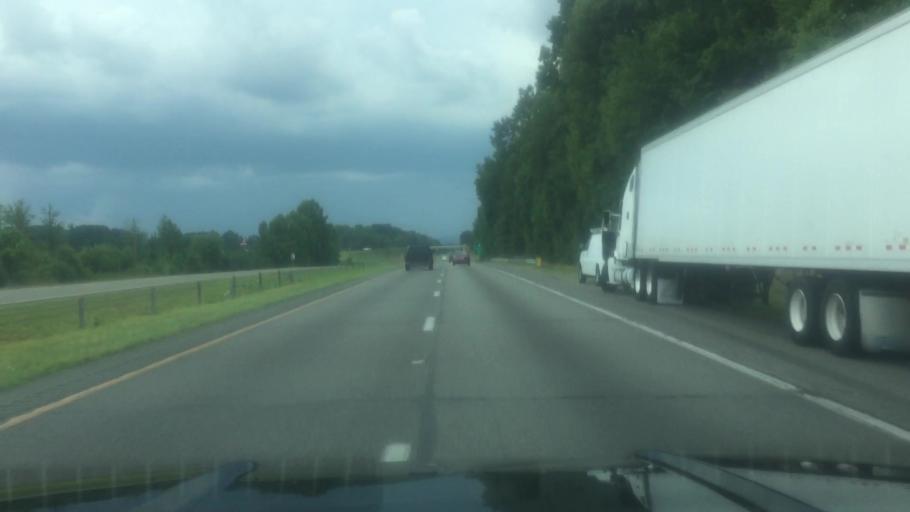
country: US
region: North Carolina
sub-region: Surry County
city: Pilot Mountain
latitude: 36.3699
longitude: -80.4837
